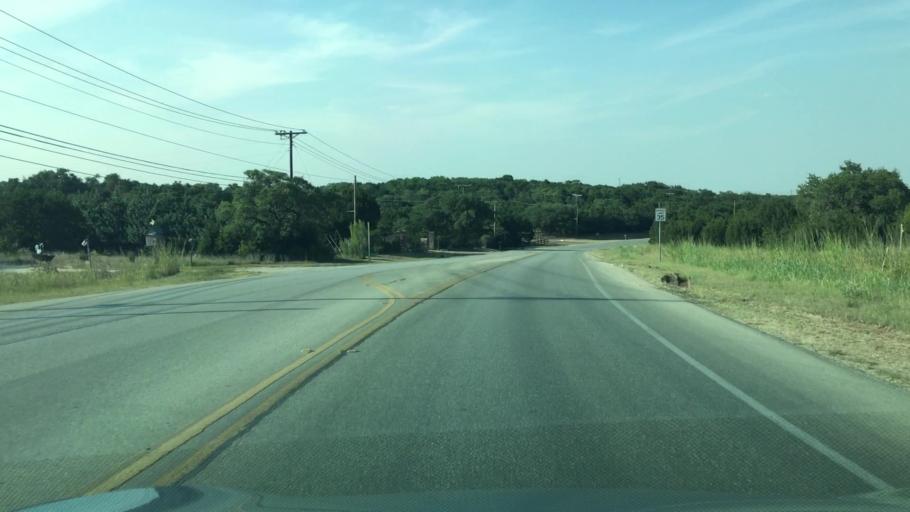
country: US
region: Texas
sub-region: Hays County
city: Dripping Springs
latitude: 30.1886
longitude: -98.0006
